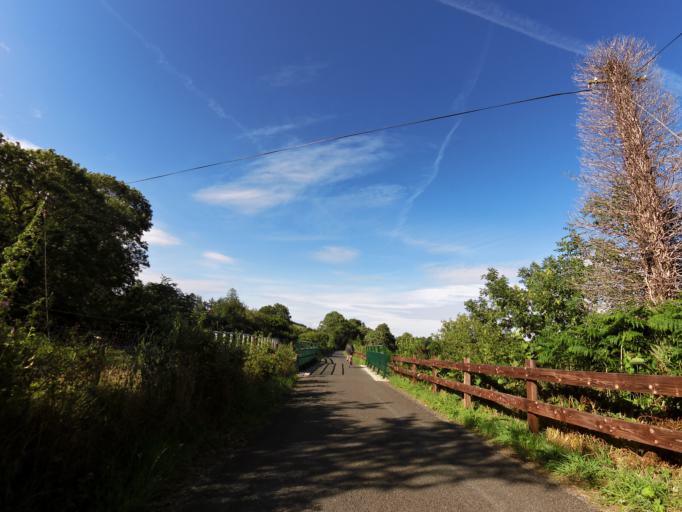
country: IE
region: Leinster
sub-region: Kilkenny
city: Mooncoin
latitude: 52.2411
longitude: -7.2651
